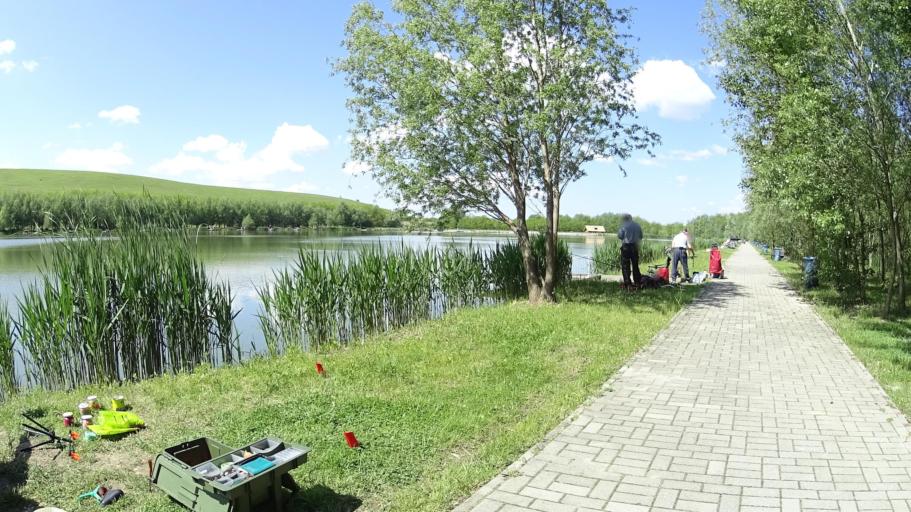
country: HU
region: Komarom-Esztergom
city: Kesztolc
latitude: 47.7002
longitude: 18.8064
